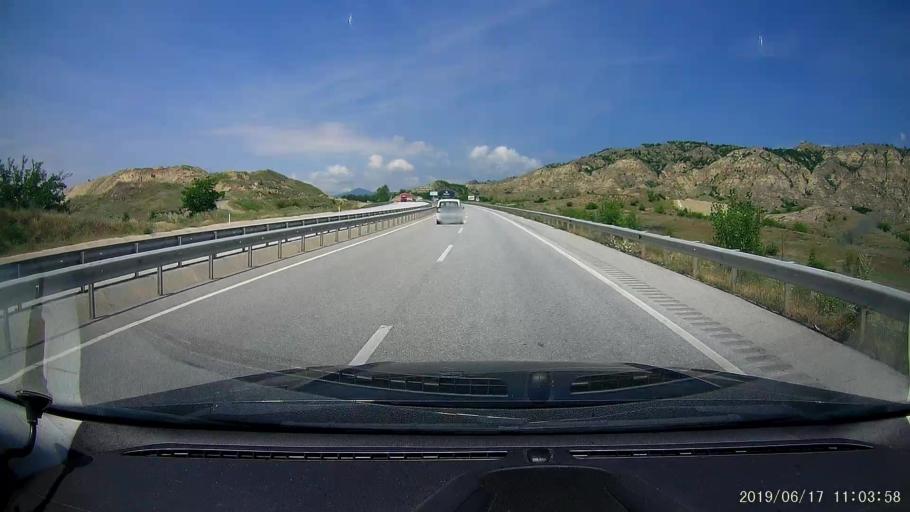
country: TR
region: Kastamonu
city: Tosya
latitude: 41.0203
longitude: 34.1048
